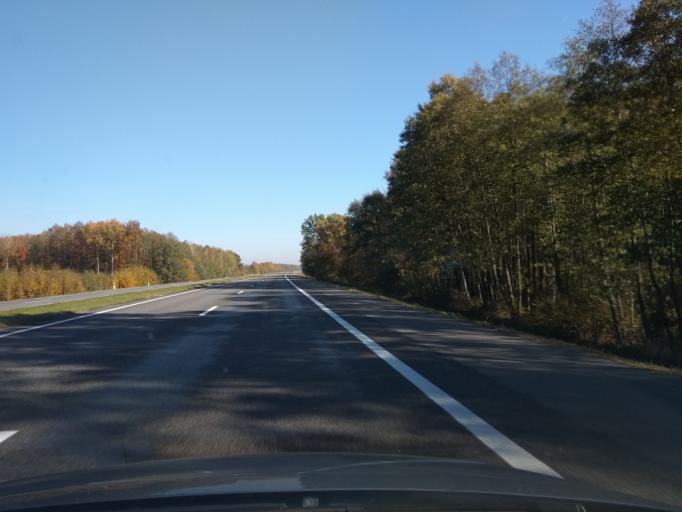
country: BY
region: Brest
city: Antopal'
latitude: 52.3420
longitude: 24.6545
